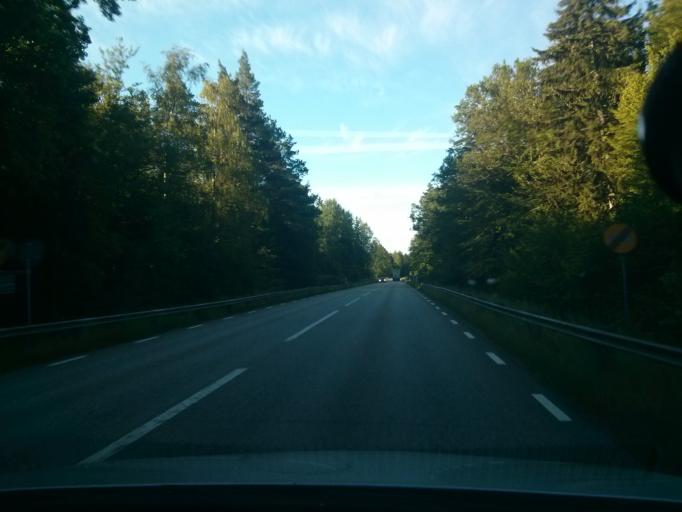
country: SE
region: Blekinge
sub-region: Ronneby Kommun
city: Brakne-Hoby
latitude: 56.3304
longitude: 15.1729
